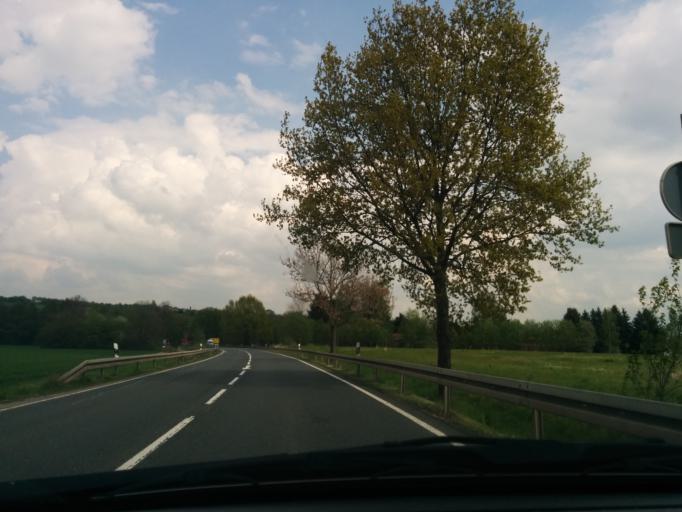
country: DE
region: Saxony
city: Niederwiesa
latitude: 50.8649
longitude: 13.0449
